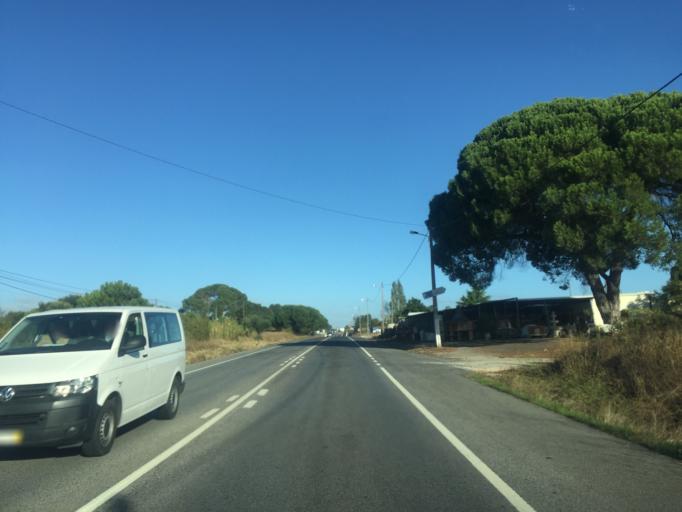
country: PT
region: Lisbon
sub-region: Azambuja
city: Aveiras de Cima
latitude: 39.1512
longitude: -8.9093
